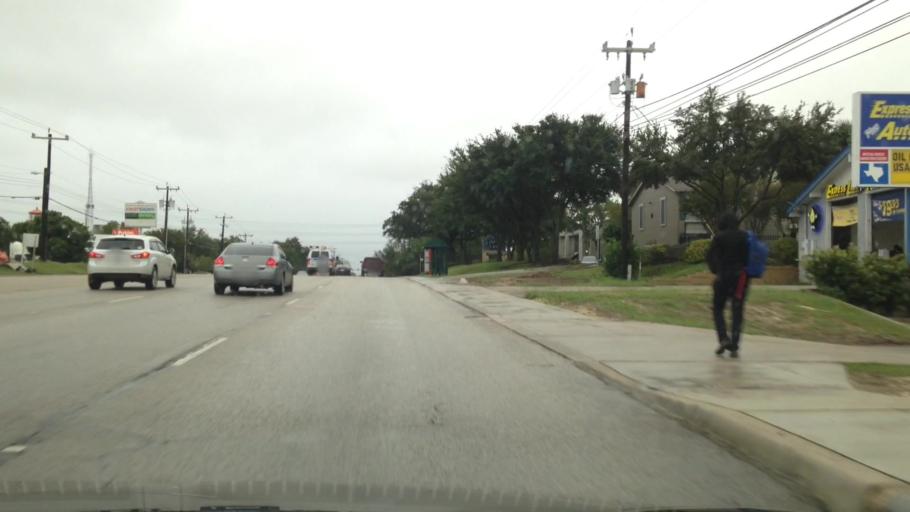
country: US
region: Texas
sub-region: Bexar County
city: Balcones Heights
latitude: 29.5250
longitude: -98.5748
